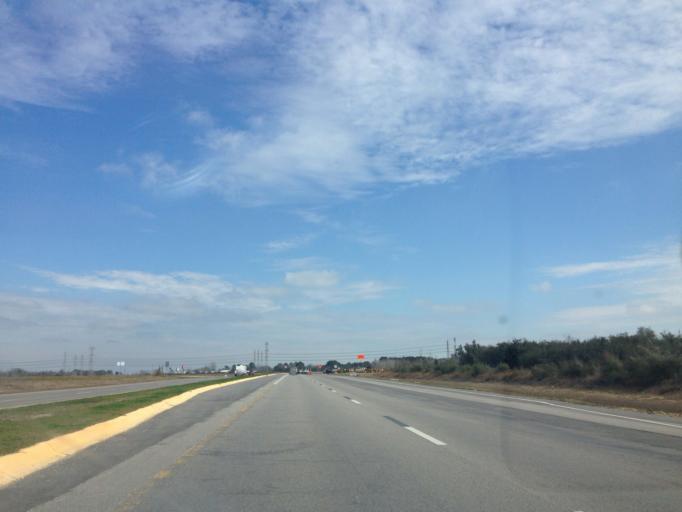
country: US
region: Texas
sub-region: Galveston County
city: Kemah
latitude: 29.5218
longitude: -95.0186
